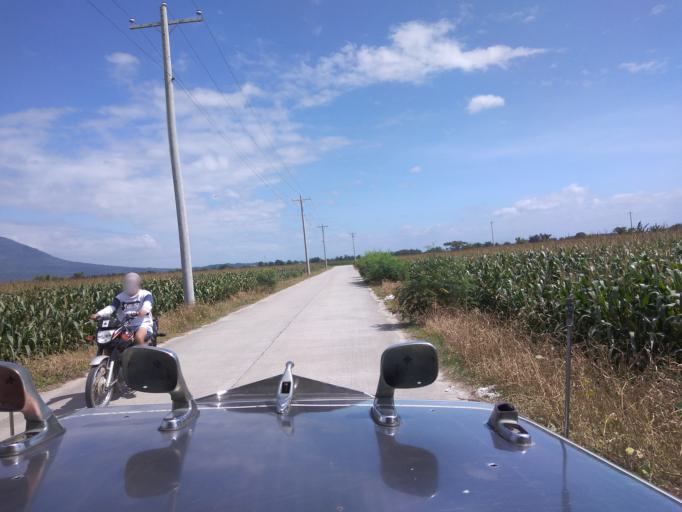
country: PH
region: Central Luzon
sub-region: Province of Pampanga
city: Anao
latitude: 15.1255
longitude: 120.7001
